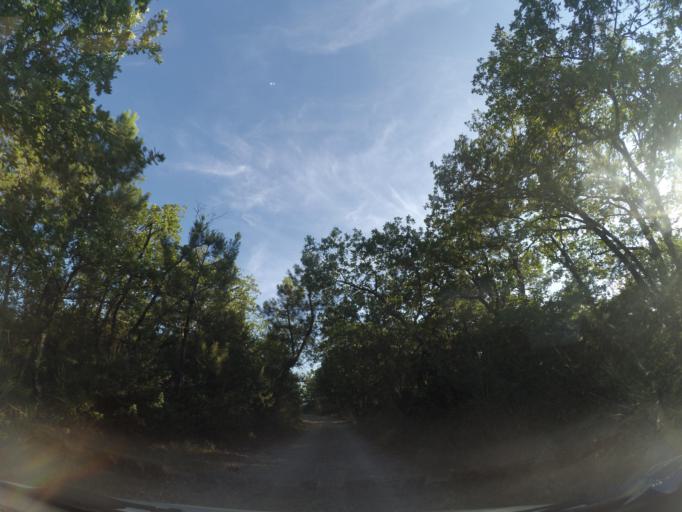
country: IT
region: Tuscany
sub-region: Province of Arezzo
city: Castiglion Fibocchi
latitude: 43.5379
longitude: 11.7875
